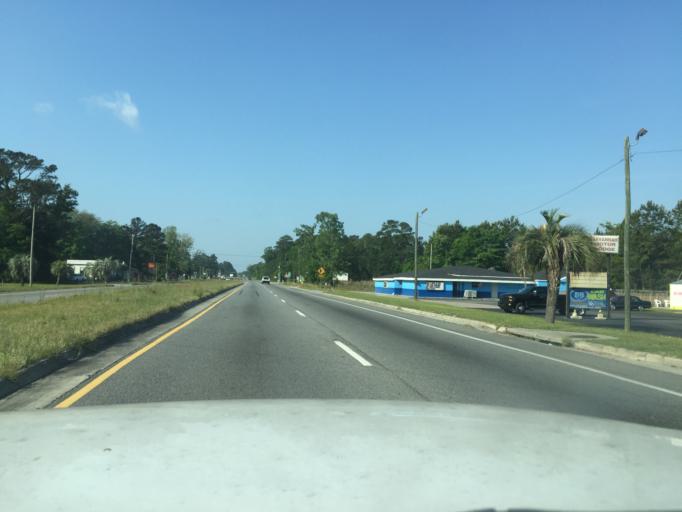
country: US
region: Georgia
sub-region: Chatham County
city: Georgetown
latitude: 32.0354
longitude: -81.2169
